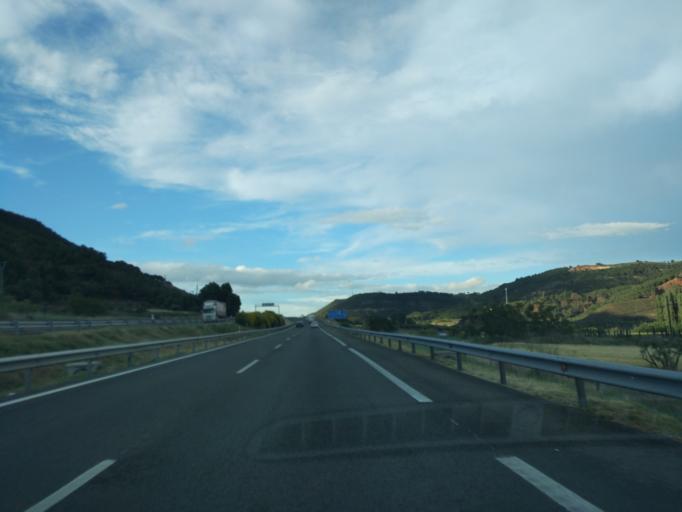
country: ES
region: Castille-La Mancha
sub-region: Provincia de Guadalajara
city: Tortola de Henares
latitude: 40.6761
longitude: -3.0989
